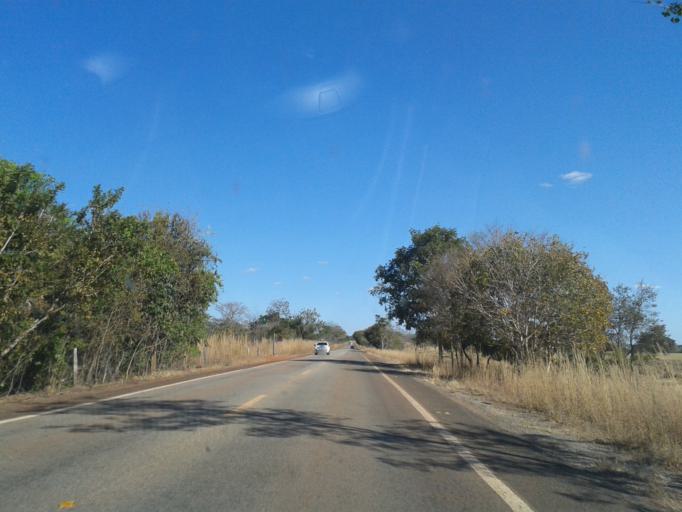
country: BR
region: Goias
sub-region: Mozarlandia
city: Mozarlandia
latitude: -14.2861
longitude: -50.4017
